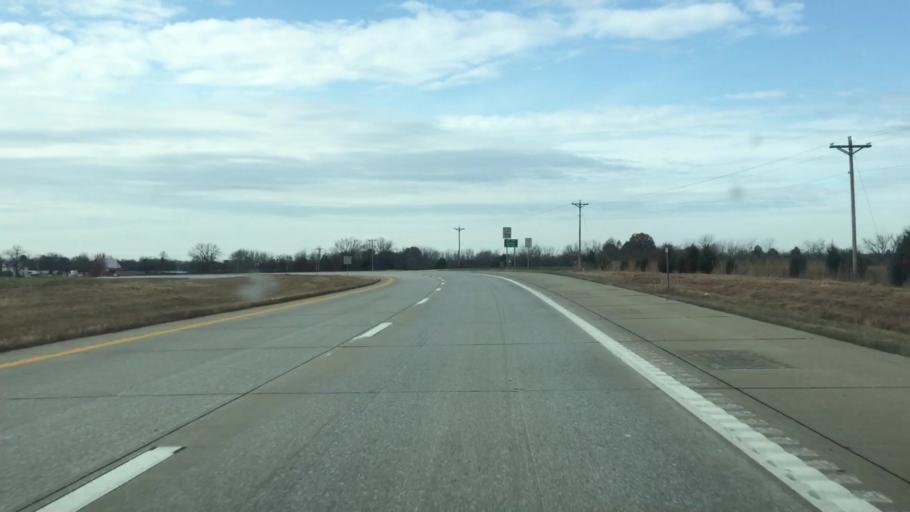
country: US
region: Missouri
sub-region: Henry County
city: Clinton
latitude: 38.4617
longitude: -93.9691
